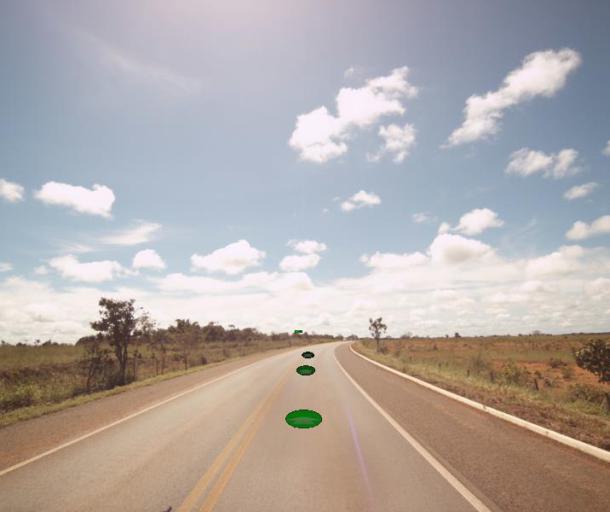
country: BR
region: Goias
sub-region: Padre Bernardo
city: Padre Bernardo
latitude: -15.1517
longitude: -48.3493
